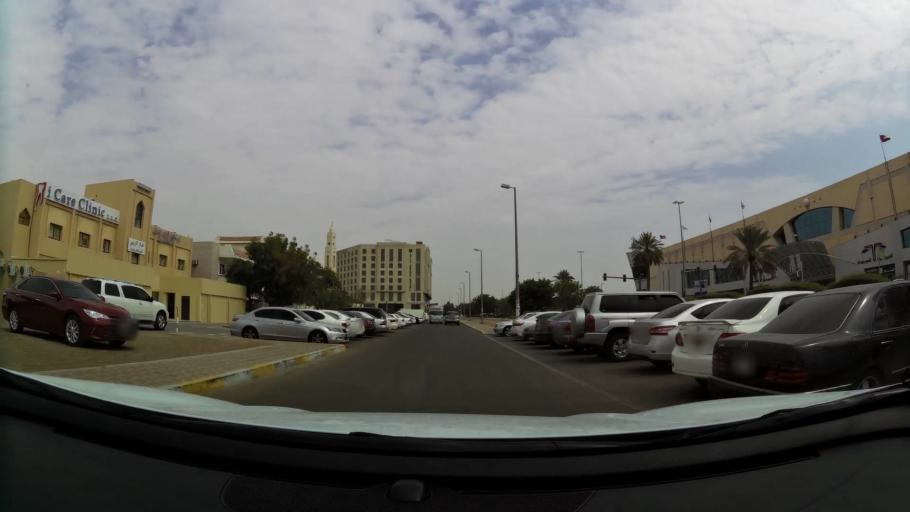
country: OM
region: Al Buraimi
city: Al Buraymi
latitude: 24.2232
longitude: 55.7811
